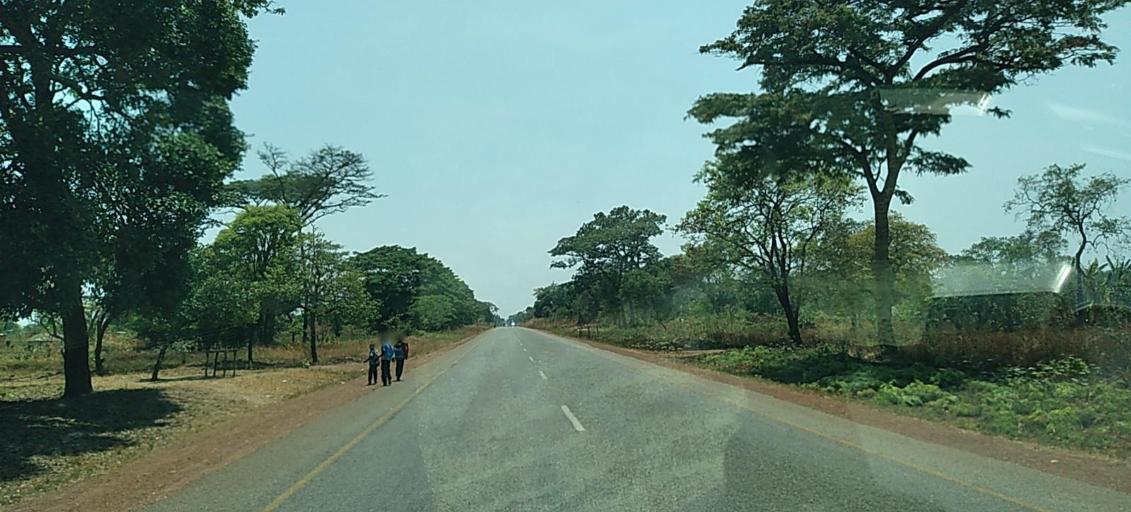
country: ZM
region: North-Western
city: Solwezi
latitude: -12.3999
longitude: 26.1511
